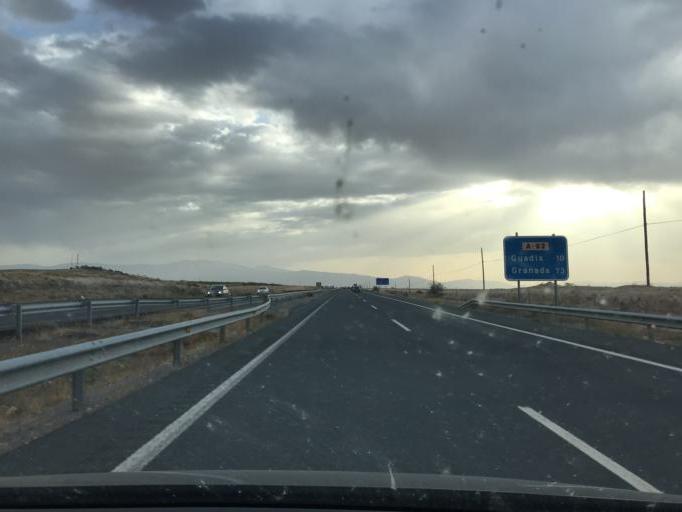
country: ES
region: Andalusia
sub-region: Provincia de Granada
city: Gor
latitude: 37.3839
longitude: -3.0518
